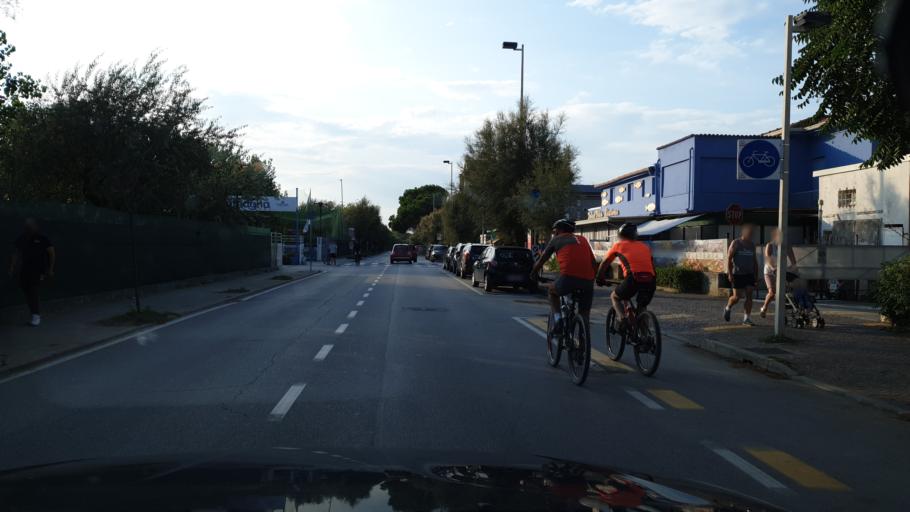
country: IT
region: Emilia-Romagna
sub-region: Provincia di Rimini
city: Misano Adriatico
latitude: 43.9892
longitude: 12.6823
